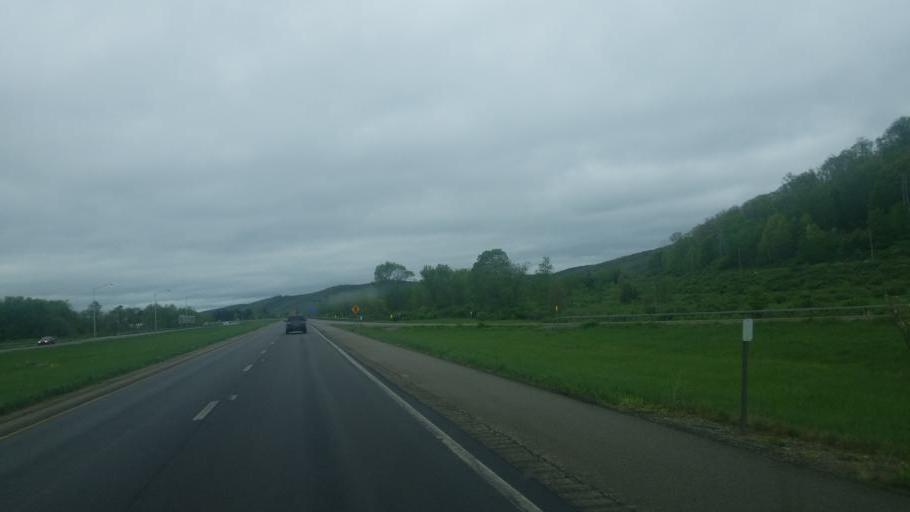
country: US
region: New York
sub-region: Cattaraugus County
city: Allegany
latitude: 42.1029
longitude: -78.5096
